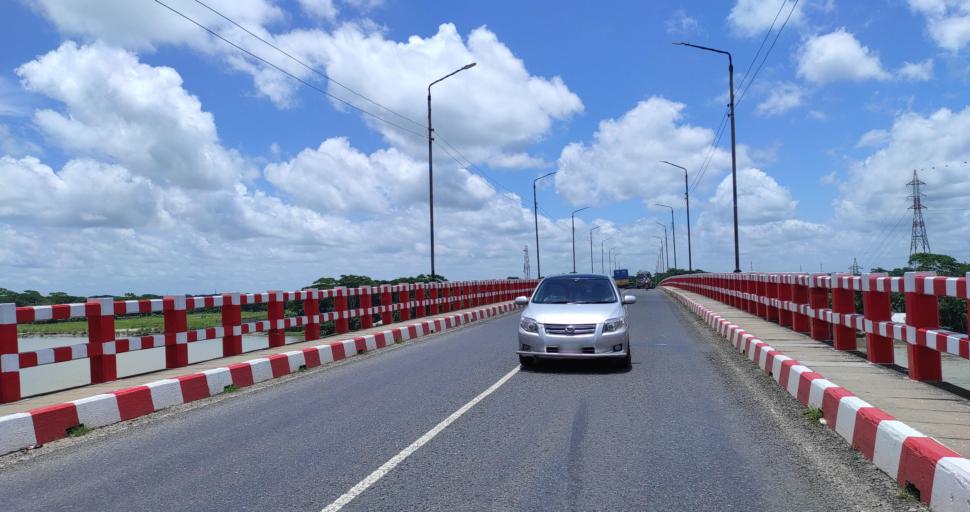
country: BD
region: Barisal
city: Gaurnadi
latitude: 22.8247
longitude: 90.2629
